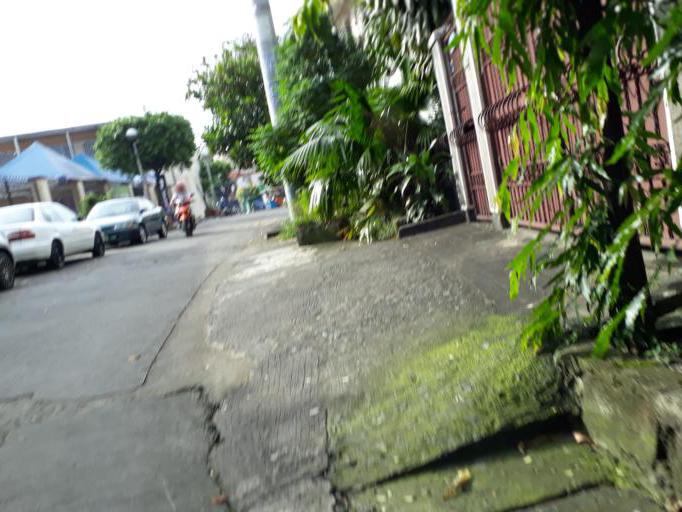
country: PH
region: Calabarzon
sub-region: Province of Rizal
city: Valenzuela
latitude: 14.6744
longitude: 120.9858
